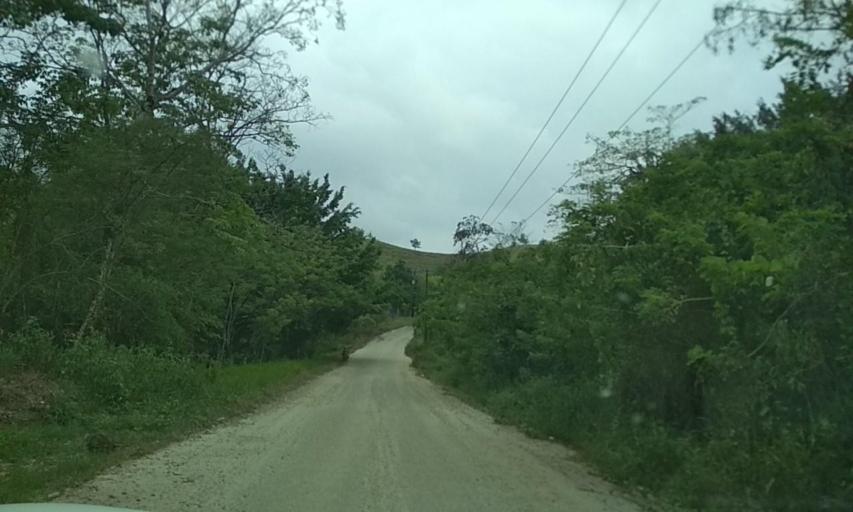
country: MX
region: Veracruz
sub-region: Uxpanapa
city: Poblado 10
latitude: 17.4952
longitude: -94.1380
